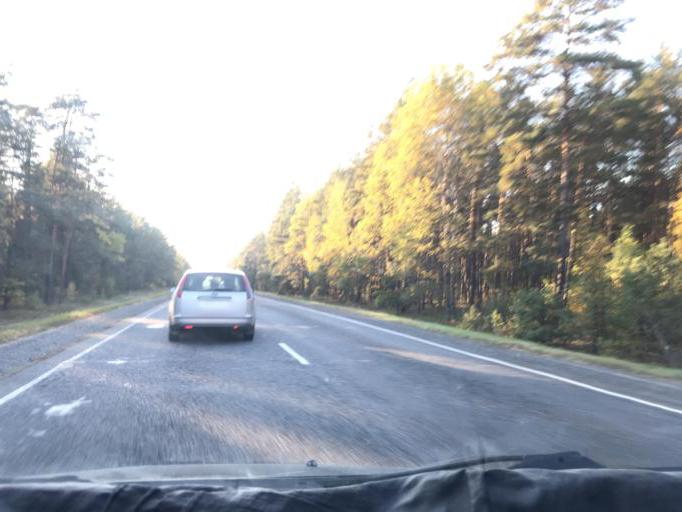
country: BY
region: Gomel
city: Zhytkavichy
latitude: 52.2727
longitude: 28.0453
